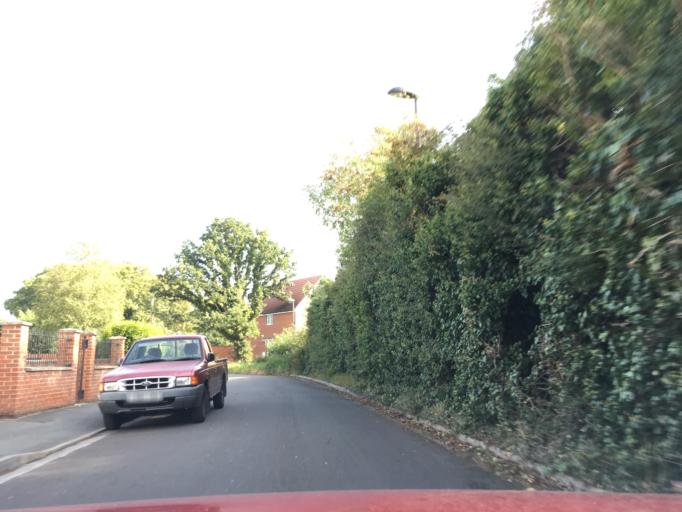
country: GB
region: England
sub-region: South Gloucestershire
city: Yate
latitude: 51.5367
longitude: -2.4228
